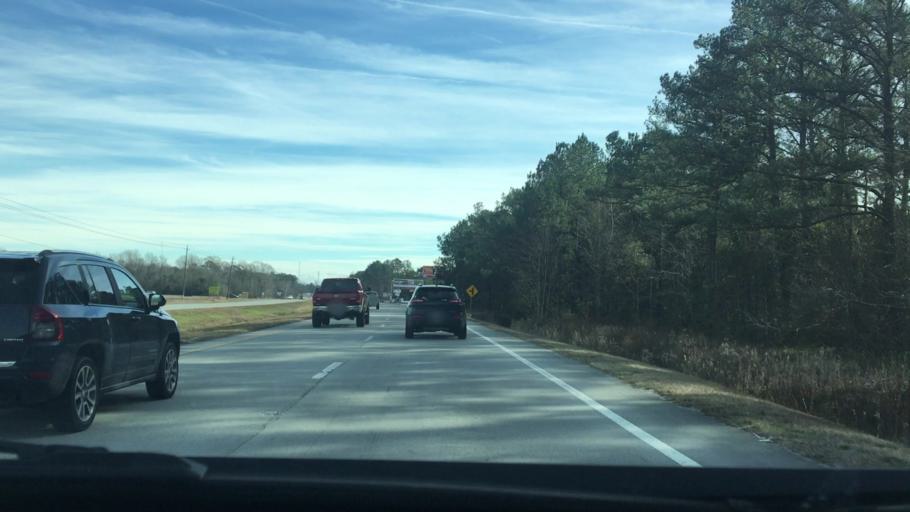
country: US
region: North Carolina
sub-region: Carteret County
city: Newport
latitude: 34.7516
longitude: -76.8419
